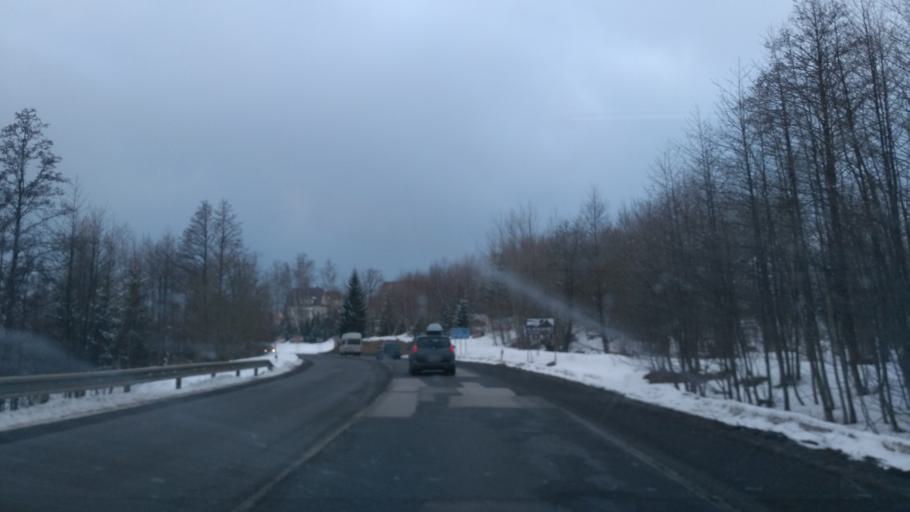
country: SK
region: Presovsky
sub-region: Okres Poprad
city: Vysoke Tatry
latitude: 49.1445
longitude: 20.2439
